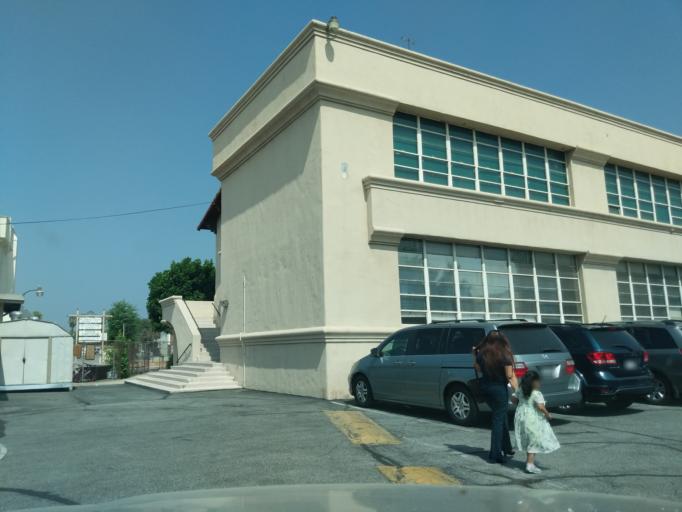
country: US
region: California
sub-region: Los Angeles County
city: San Gabriel
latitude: 34.0983
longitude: -118.1072
